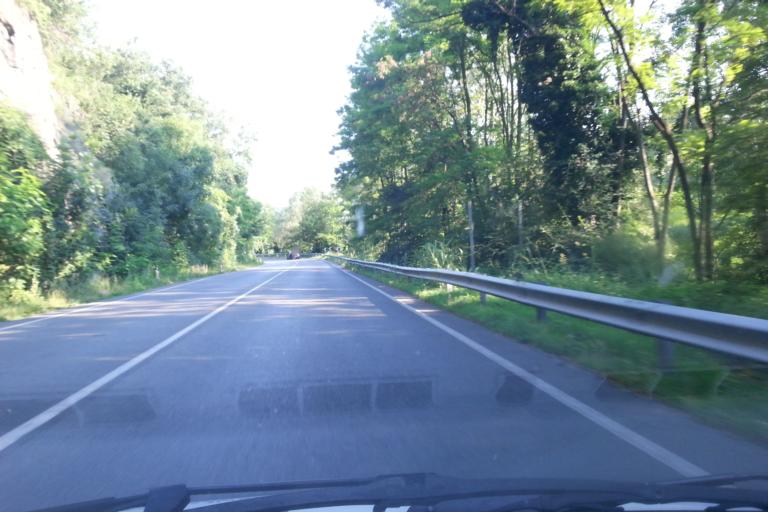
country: IT
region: Piedmont
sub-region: Provincia di Torino
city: Sant'Ambrogio di Torino
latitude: 45.1062
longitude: 7.3711
